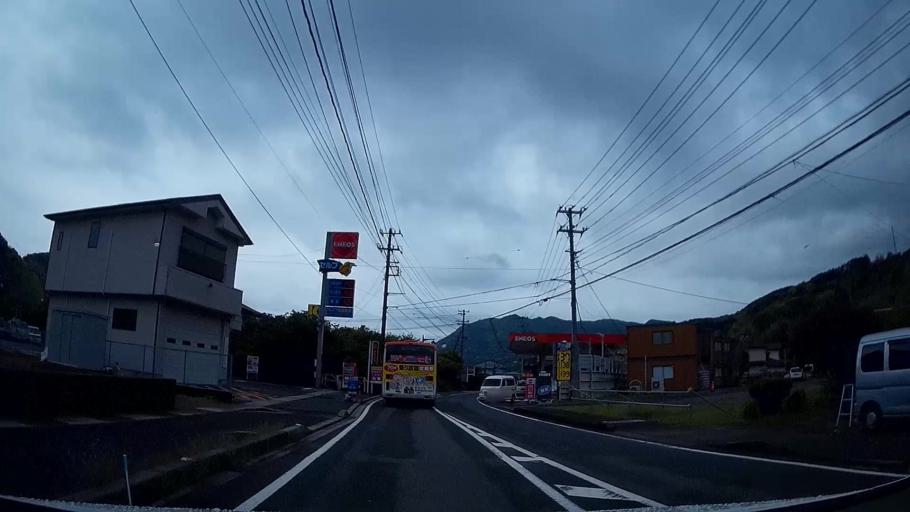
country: JP
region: Shizuoka
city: Shimoda
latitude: 34.7610
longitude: 138.9821
